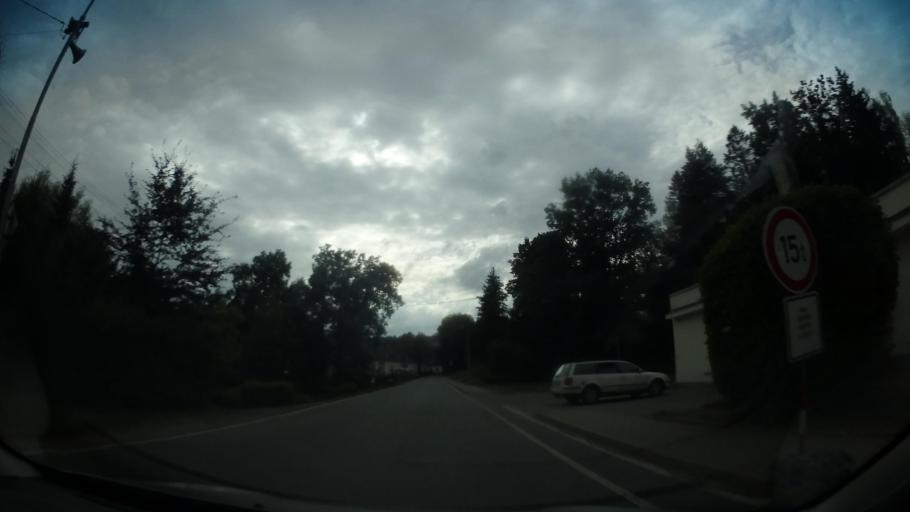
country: CZ
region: Pardubicky
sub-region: Okres Chrudim
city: Nasavrky
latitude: 49.8034
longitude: 15.7420
